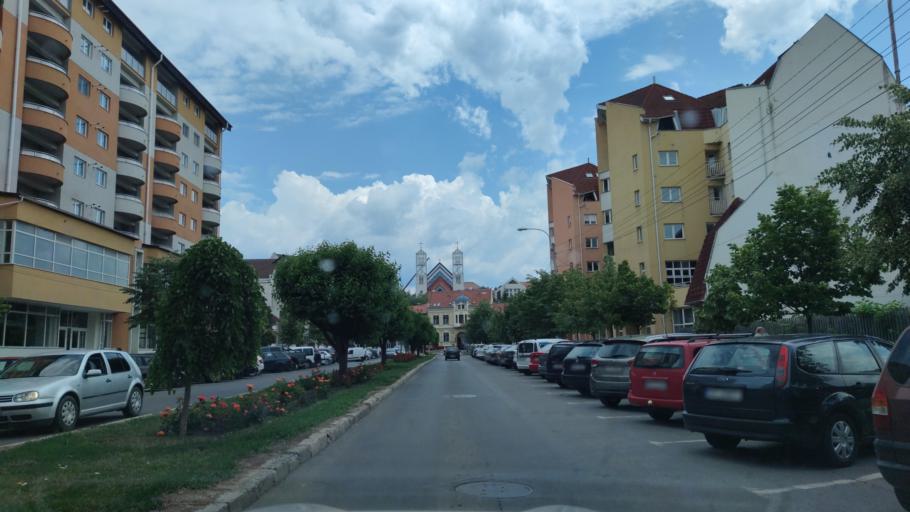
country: RO
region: Harghita
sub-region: Municipiul Miercurea Ciuc
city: Miercurea-Ciuc
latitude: 46.3624
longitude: 25.8043
